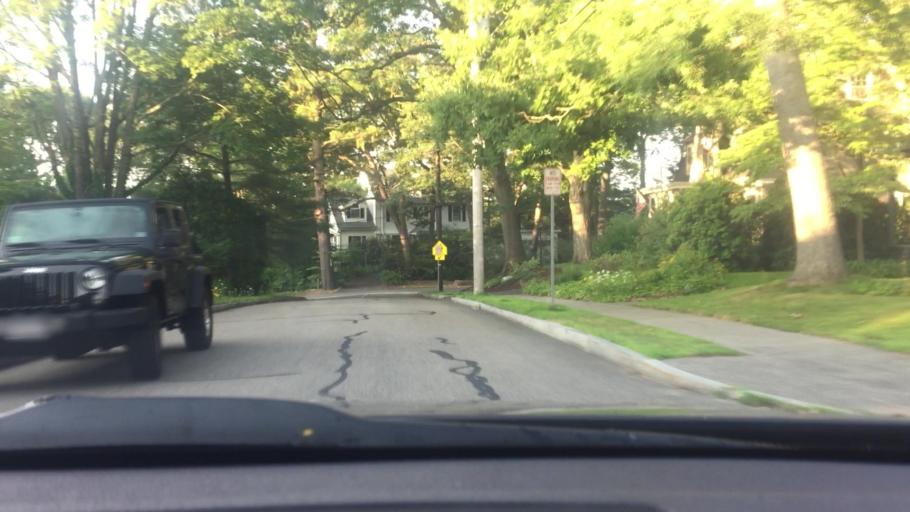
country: US
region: Massachusetts
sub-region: Norfolk County
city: Needham
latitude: 42.2767
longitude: -71.2287
